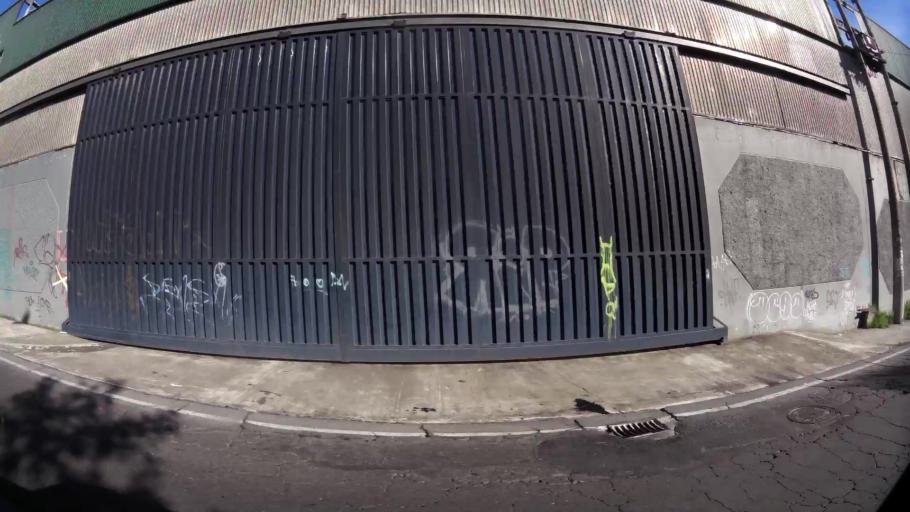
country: EC
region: Pichincha
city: Quito
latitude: -0.2906
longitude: -78.5391
